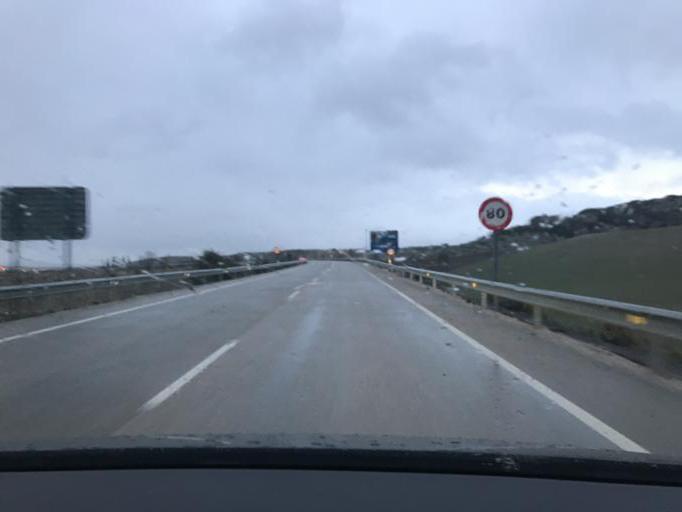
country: ES
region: Andalusia
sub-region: Provincia de Granada
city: Campotejar
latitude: 37.4695
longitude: -3.5753
